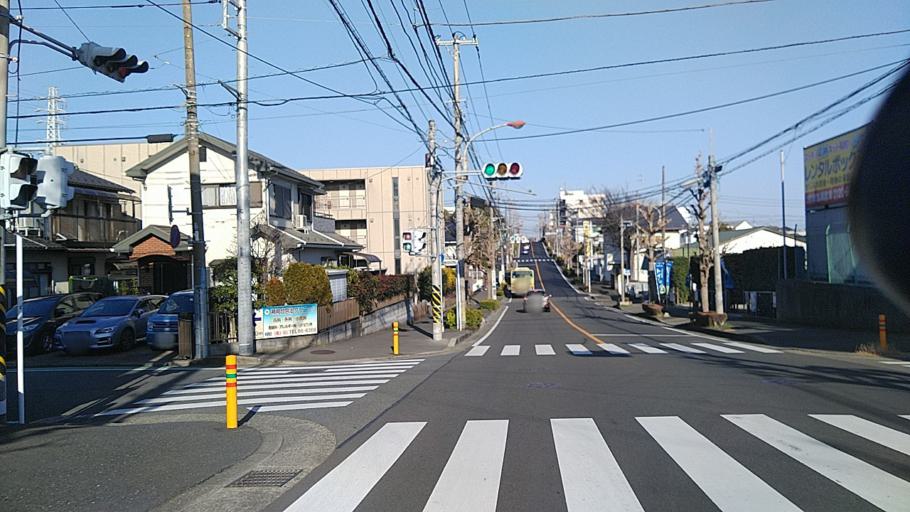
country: JP
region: Kanagawa
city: Fujisawa
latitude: 35.3820
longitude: 139.4524
